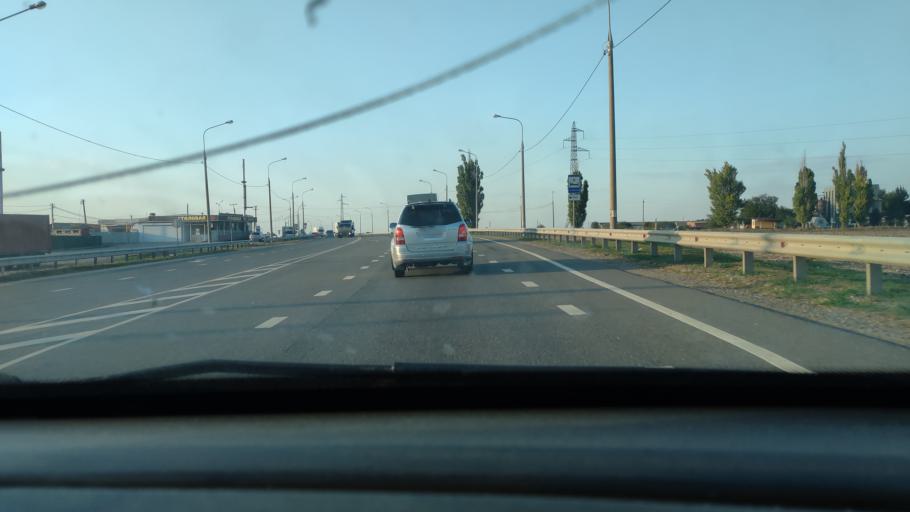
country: RU
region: Krasnodarskiy
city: Kanevskaya
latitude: 46.0751
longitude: 39.0147
